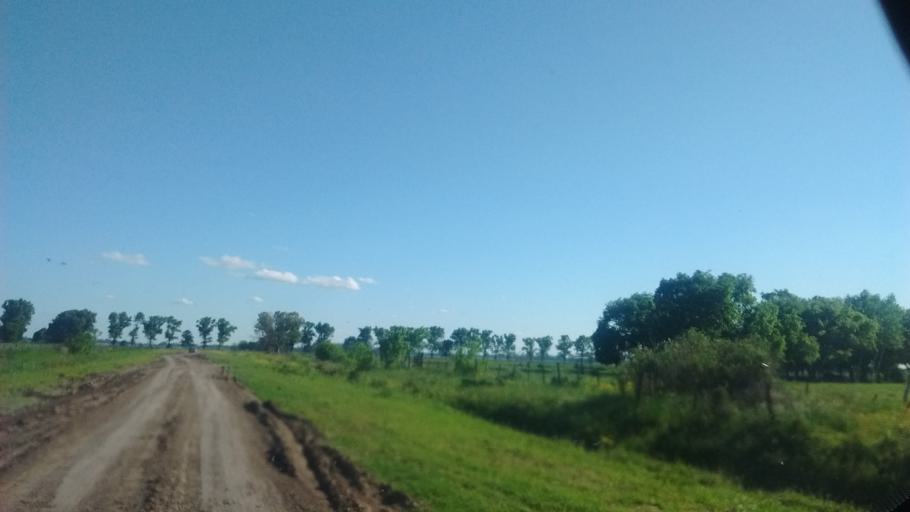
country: AR
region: Santa Fe
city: Funes
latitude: -32.8692
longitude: -60.7985
